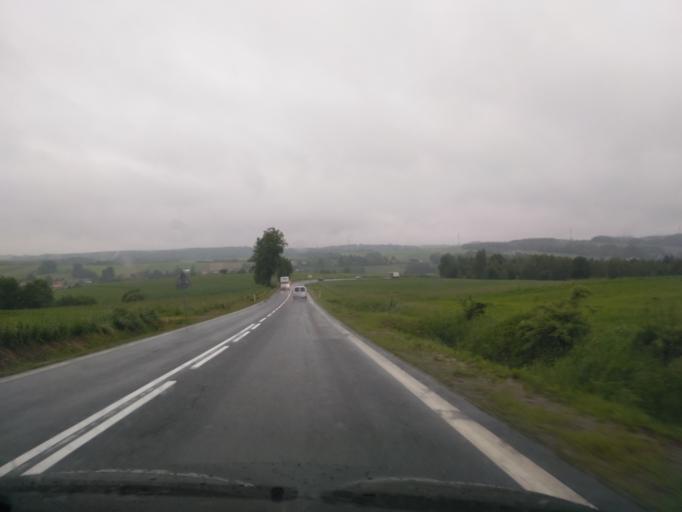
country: PL
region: Subcarpathian Voivodeship
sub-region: Powiat strzyzowski
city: Frysztak
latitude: 49.7934
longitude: 21.5730
